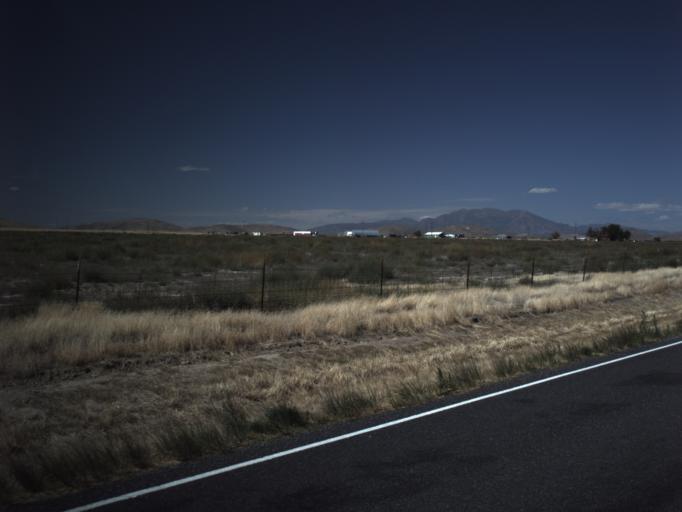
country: US
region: Utah
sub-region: Utah County
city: Genola
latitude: 40.0504
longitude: -111.9583
